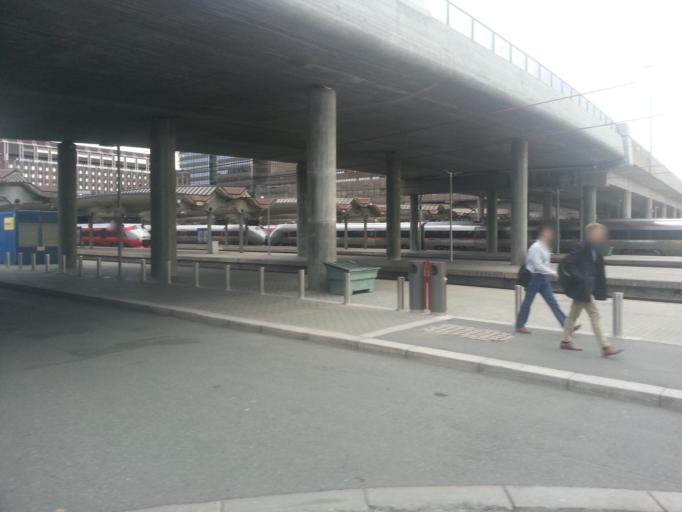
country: NO
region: Oslo
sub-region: Oslo
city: Oslo
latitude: 59.9092
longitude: 10.7567
